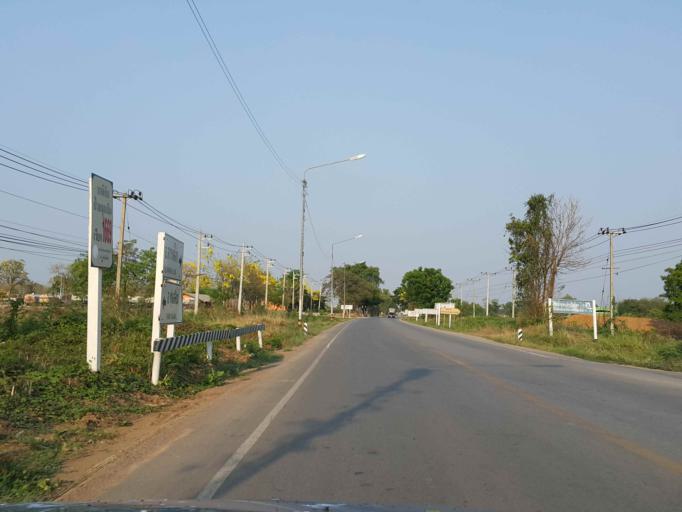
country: TH
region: Sukhothai
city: Sawankhalok
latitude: 17.3097
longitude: 99.7940
